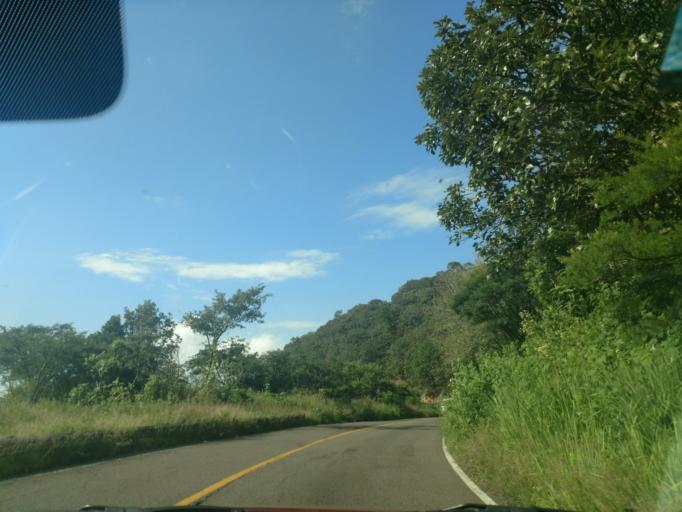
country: MX
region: Jalisco
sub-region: Atengo
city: Soyatlan del Oro
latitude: 20.4894
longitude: -104.3612
